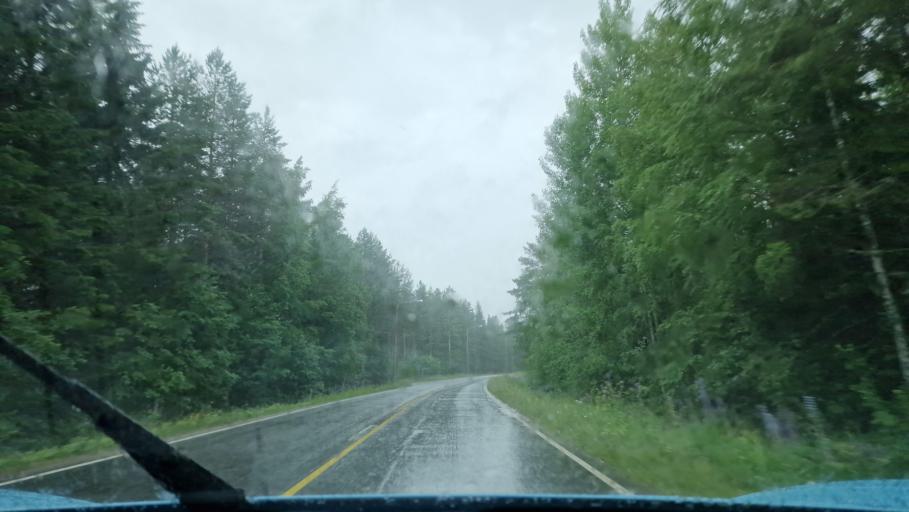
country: FI
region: Southern Ostrobothnia
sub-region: Jaerviseutu
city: Soini
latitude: 62.8347
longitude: 24.3326
